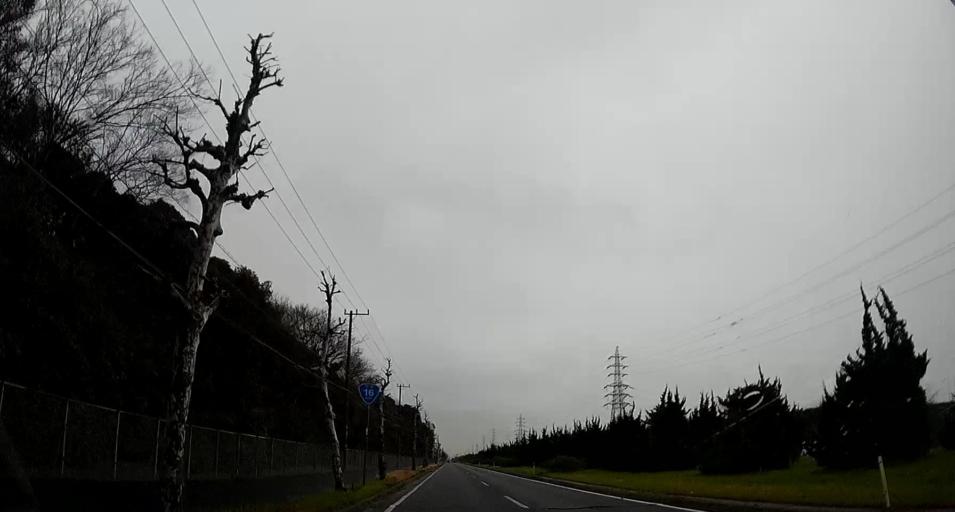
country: JP
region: Chiba
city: Ichihara
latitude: 35.5116
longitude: 140.0564
